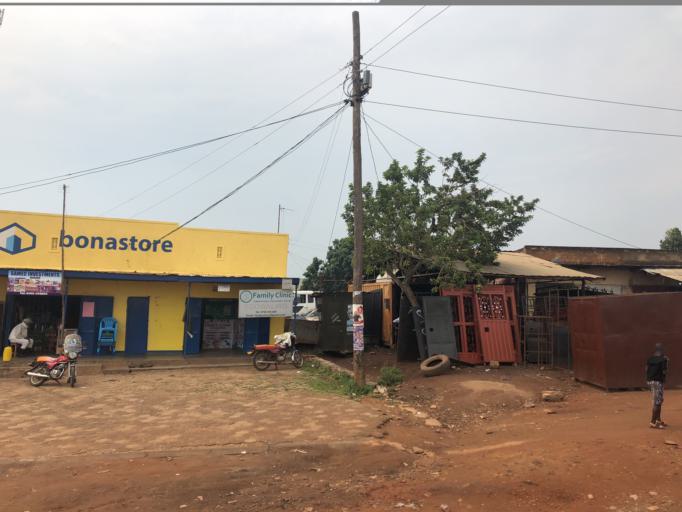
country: UG
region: Central Region
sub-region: Mukono District
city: Mukono
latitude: 0.3519
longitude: 32.7595
